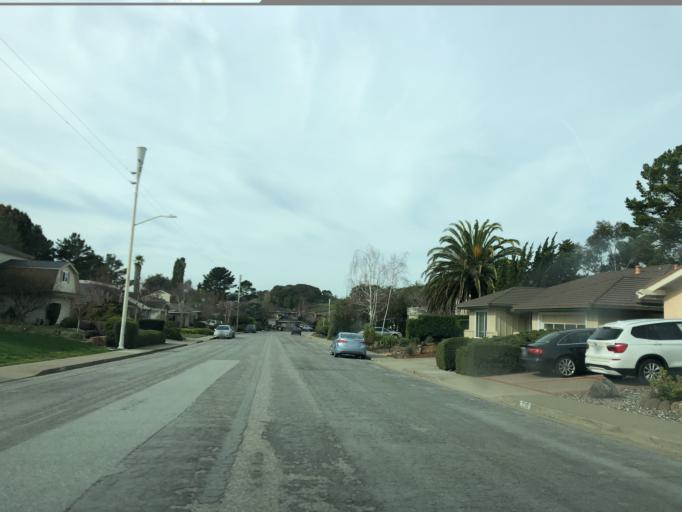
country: US
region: California
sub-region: San Mateo County
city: Highlands-Baywood Park
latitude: 37.5034
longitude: -122.3163
